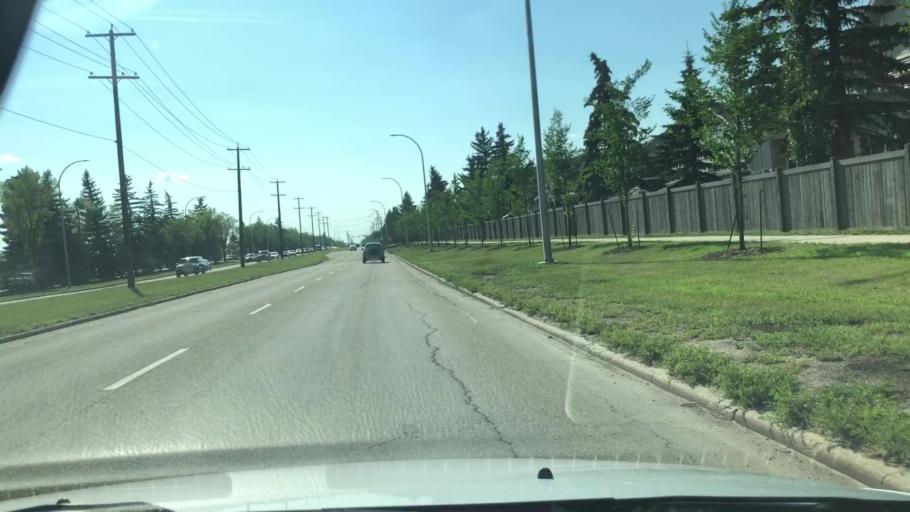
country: CA
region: Alberta
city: Edmonton
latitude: 53.5996
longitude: -113.5087
